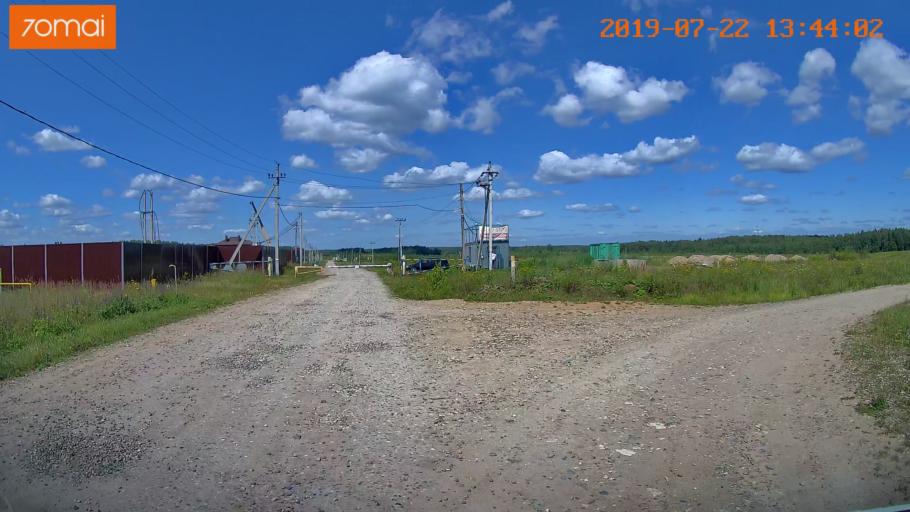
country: RU
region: Ivanovo
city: Novo-Talitsy
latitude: 57.0849
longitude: 40.8728
